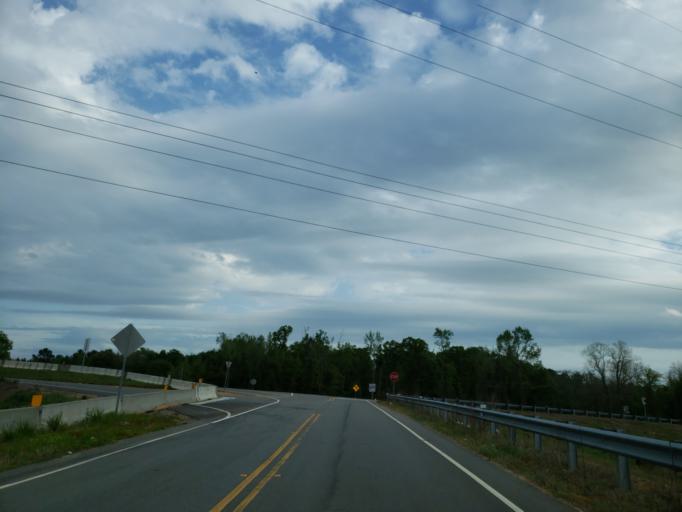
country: US
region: Georgia
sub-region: Dooly County
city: Vienna
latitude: 32.1230
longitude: -83.7648
